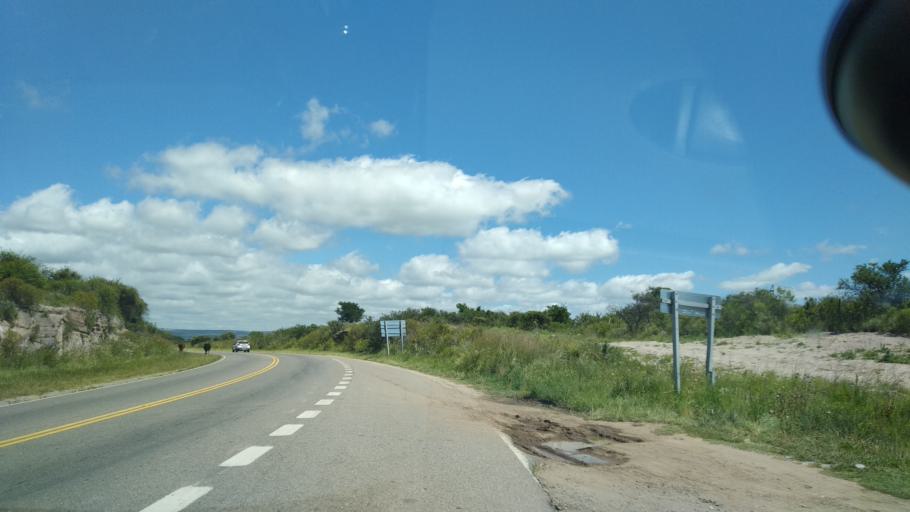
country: AR
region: Cordoba
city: Villa Cura Brochero
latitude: -31.6943
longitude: -65.0605
